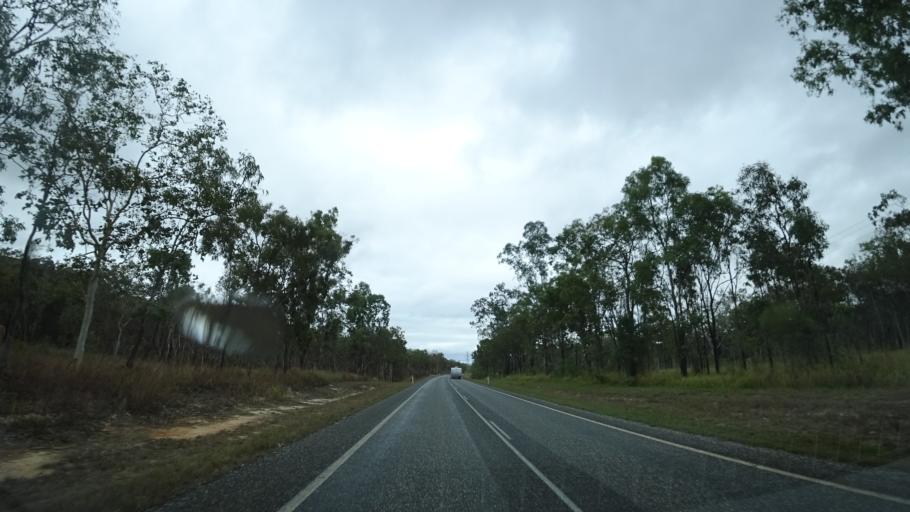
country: AU
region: Queensland
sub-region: Tablelands
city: Mareeba
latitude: -16.7349
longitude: 145.3509
